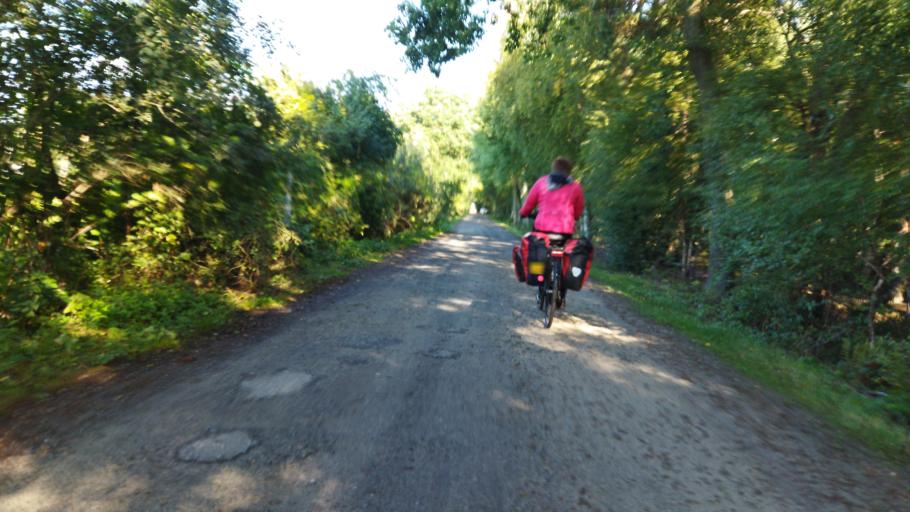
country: DE
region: Lower Saxony
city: Ohne
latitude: 52.2853
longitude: 7.3154
